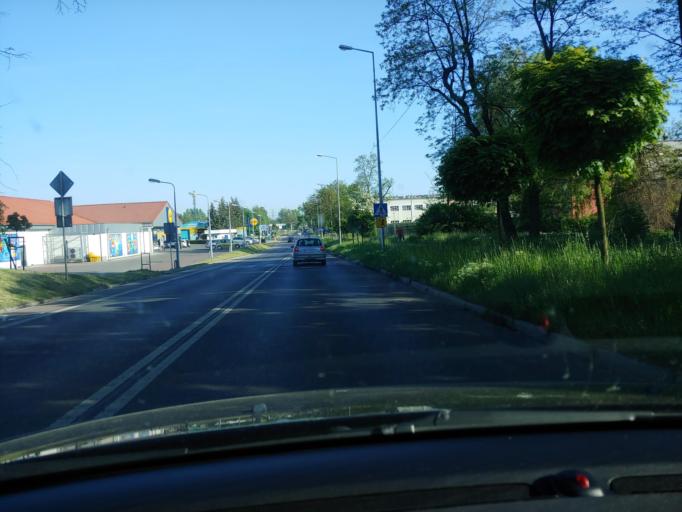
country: PL
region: Silesian Voivodeship
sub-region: Jaworzno
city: Jaworzno
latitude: 50.1952
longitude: 19.2825
